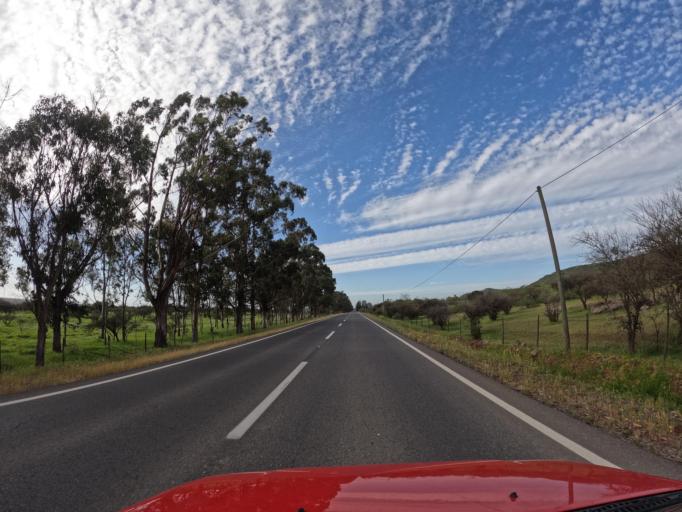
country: CL
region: O'Higgins
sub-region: Provincia de Colchagua
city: Santa Cruz
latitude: -34.1800
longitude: -71.7326
